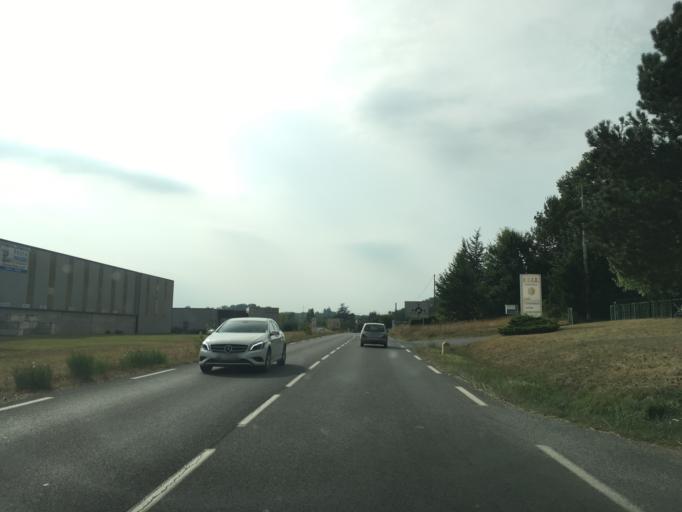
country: FR
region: Aquitaine
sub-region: Departement de la Dordogne
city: Carsac-Aillac
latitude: 44.8632
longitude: 1.2590
